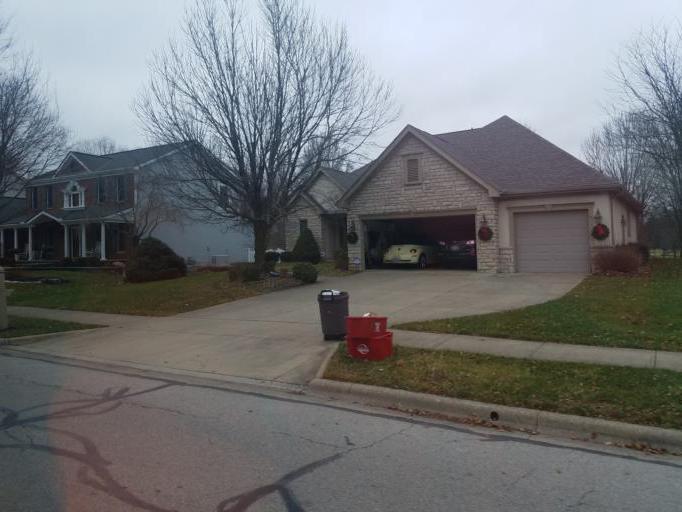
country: US
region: Ohio
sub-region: Franklin County
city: Westerville
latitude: 40.1296
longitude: -82.9493
